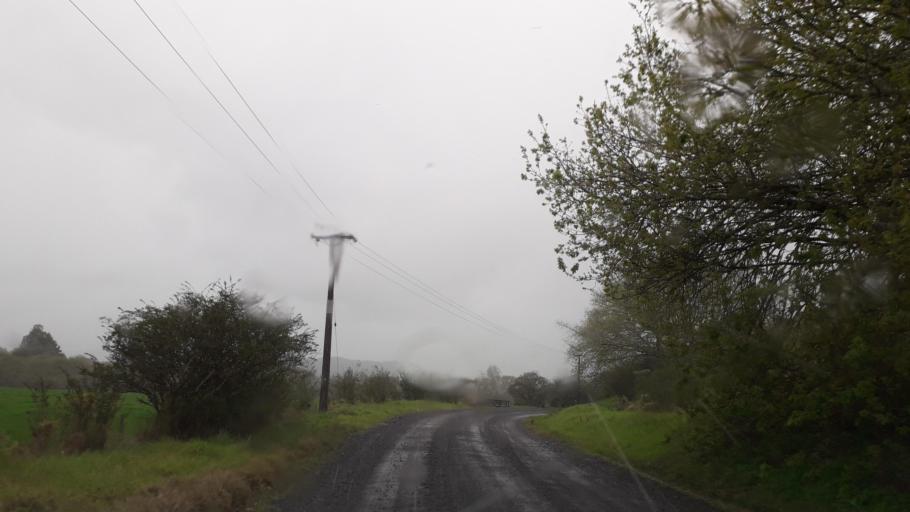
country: NZ
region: Northland
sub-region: Far North District
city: Waimate North
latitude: -35.4853
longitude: 173.7005
